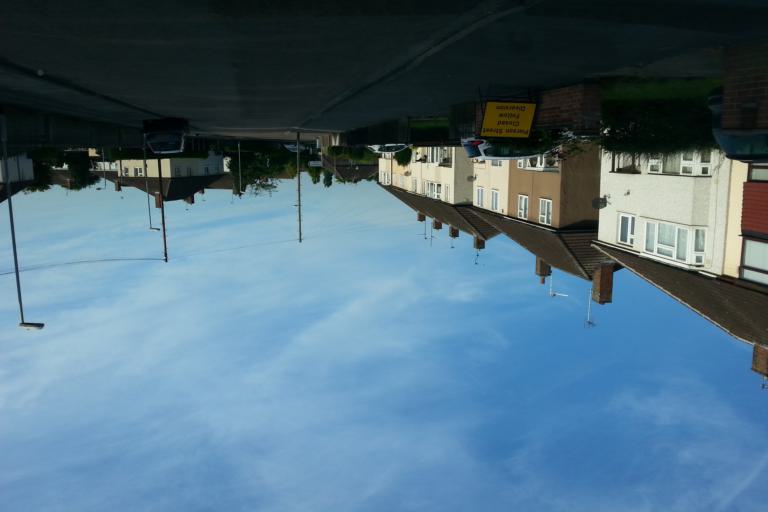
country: GB
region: England
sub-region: Nottinghamshire
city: Newark on Trent
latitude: 53.0625
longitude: -0.8170
